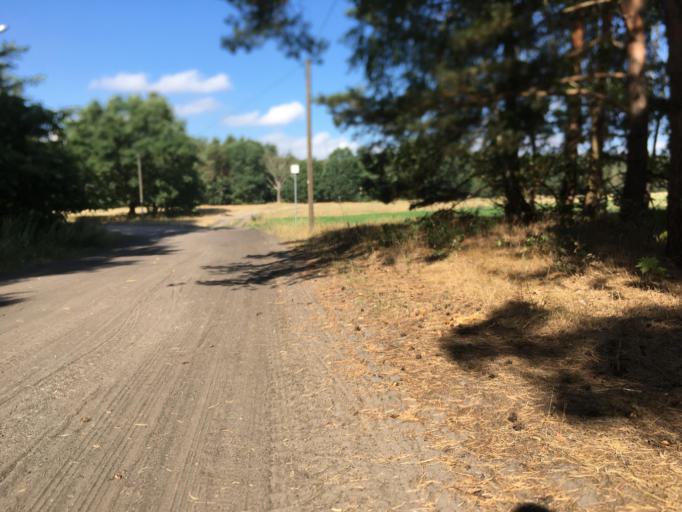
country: DE
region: Brandenburg
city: Zehdenick
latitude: 52.9471
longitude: 13.3959
